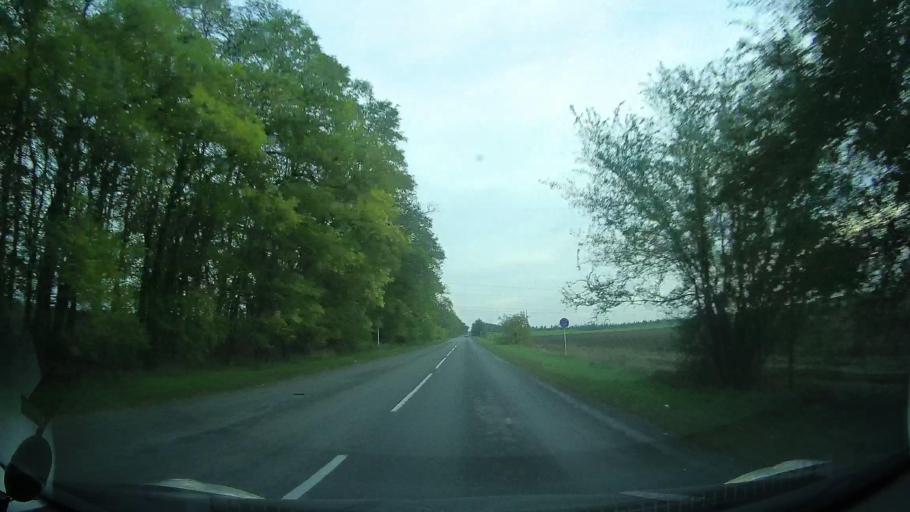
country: RU
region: Rostov
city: Ol'ginskaya
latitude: 47.1124
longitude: 39.9772
